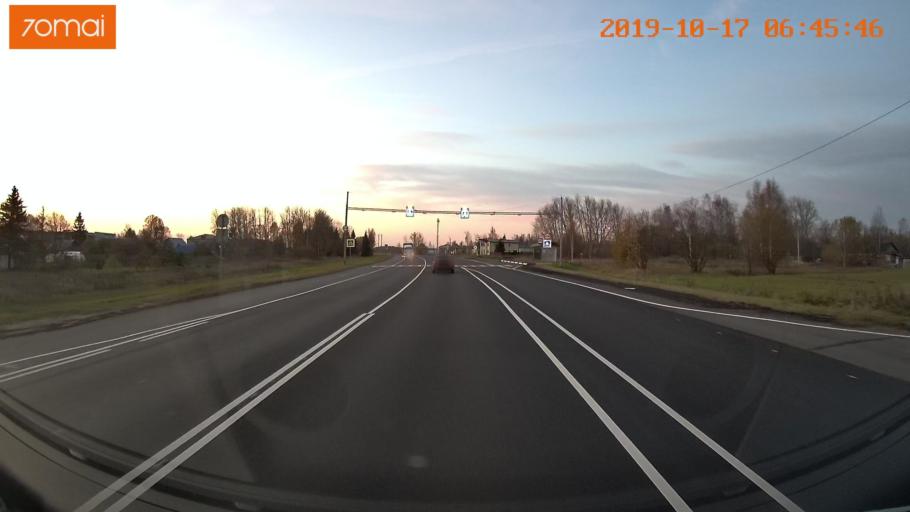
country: RU
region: Vladimir
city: Kideksha
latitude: 56.5563
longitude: 40.5477
